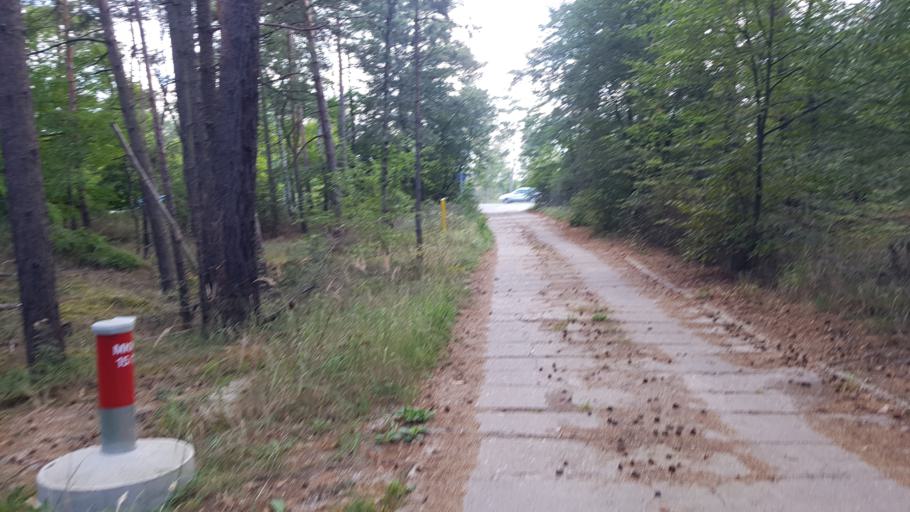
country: DE
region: Brandenburg
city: Sonnewalde
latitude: 51.6349
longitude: 13.6482
